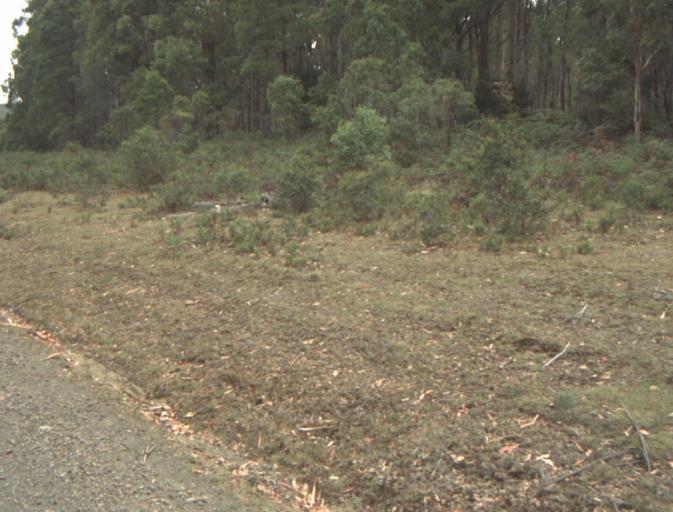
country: AU
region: Tasmania
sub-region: Dorset
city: Scottsdale
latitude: -41.4335
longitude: 147.5151
